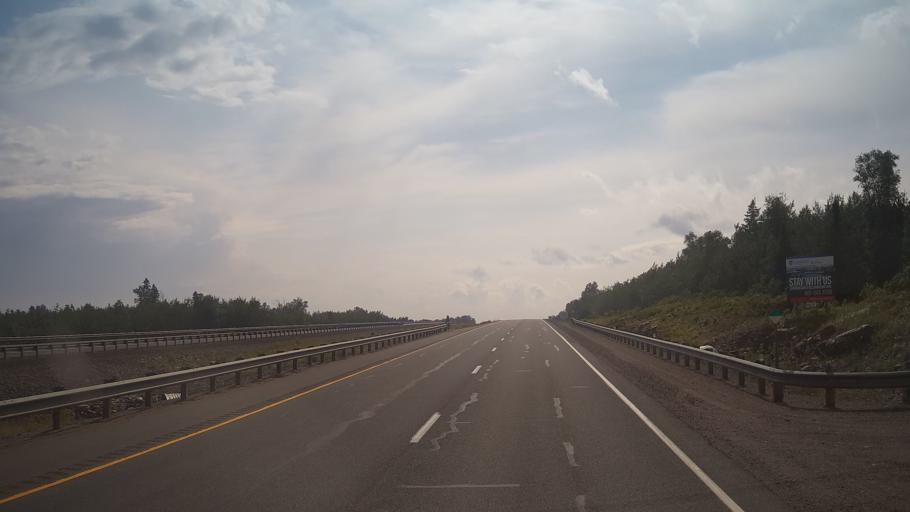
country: CA
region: Ontario
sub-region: Thunder Bay District
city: Thunder Bay
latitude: 48.5662
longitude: -88.8582
